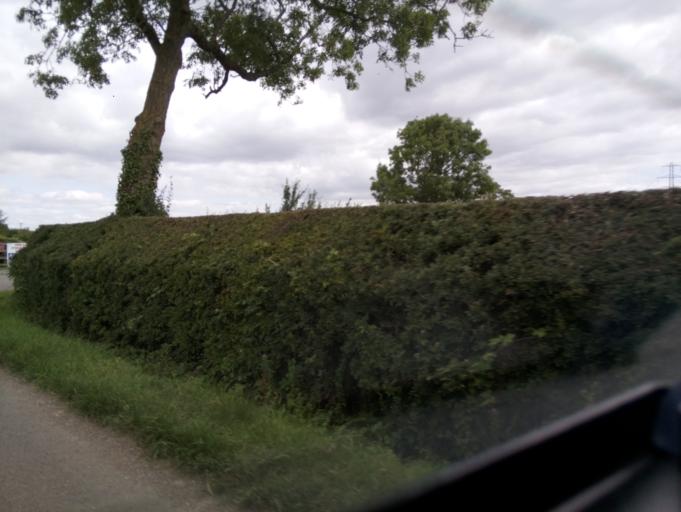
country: GB
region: England
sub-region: Buckinghamshire
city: Newton Longville
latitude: 51.9702
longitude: -0.8180
